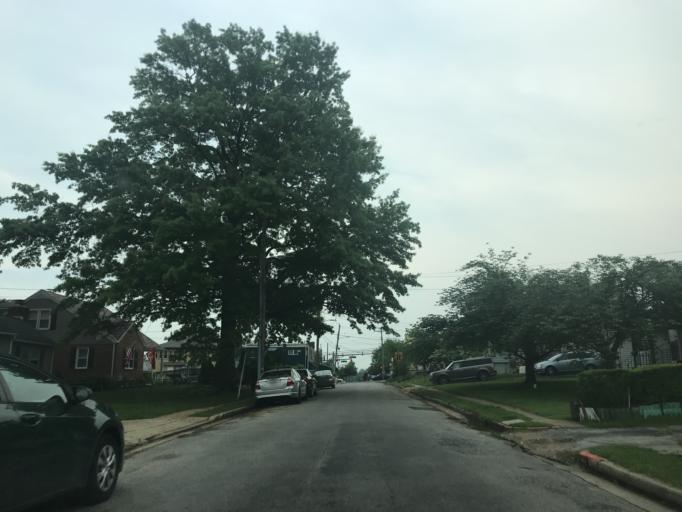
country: US
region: Maryland
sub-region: Baltimore County
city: Parkville
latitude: 39.3799
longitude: -76.5399
